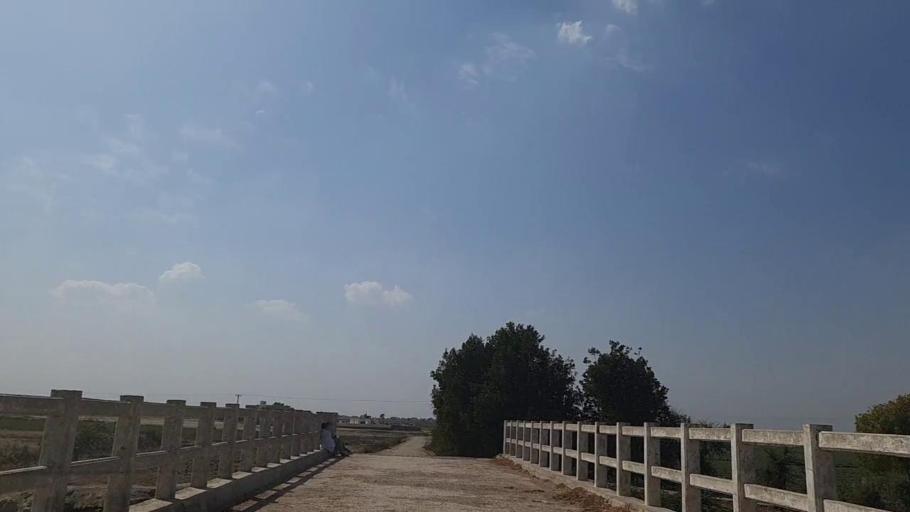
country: PK
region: Sindh
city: Jati
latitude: 24.4785
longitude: 68.2688
